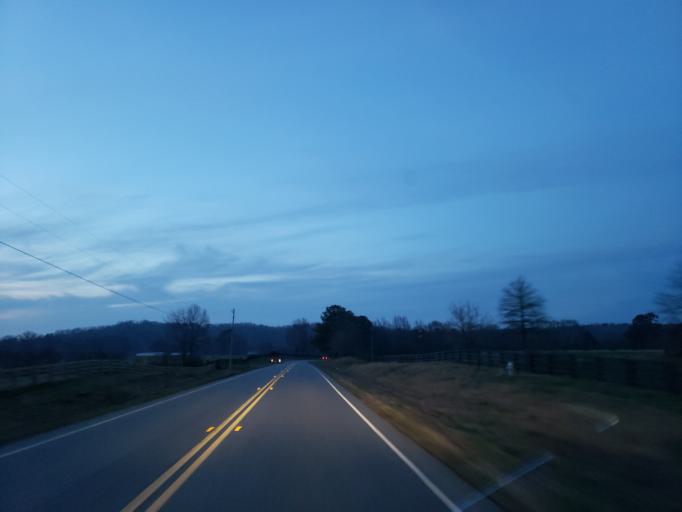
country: US
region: Georgia
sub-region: Cherokee County
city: Ball Ground
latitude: 34.2946
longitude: -84.2748
